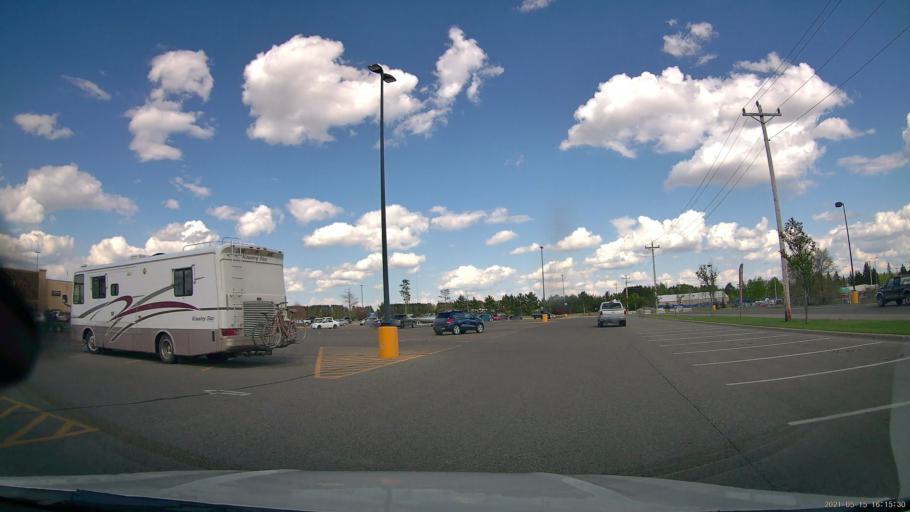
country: US
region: Minnesota
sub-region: Hubbard County
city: Park Rapids
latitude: 46.9239
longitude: -95.0343
